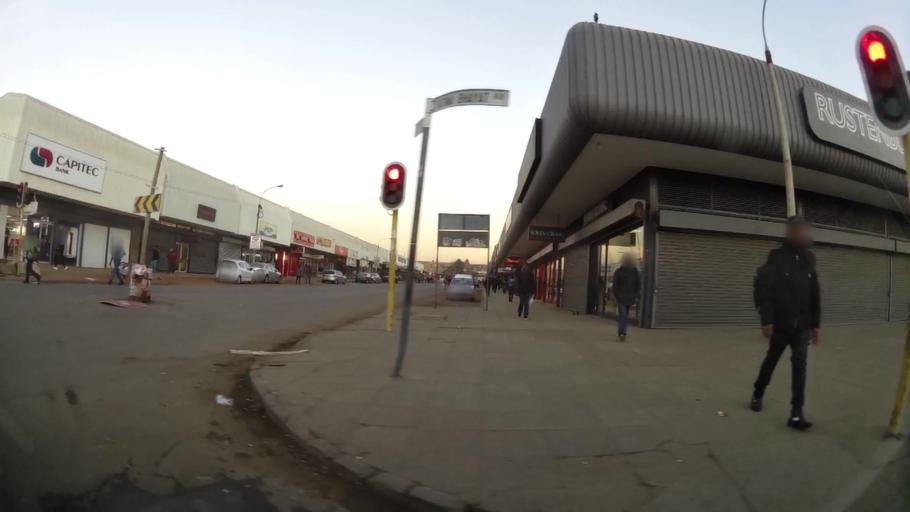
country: ZA
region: North-West
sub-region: Bojanala Platinum District Municipality
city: Rustenburg
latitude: -25.6656
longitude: 27.2393
